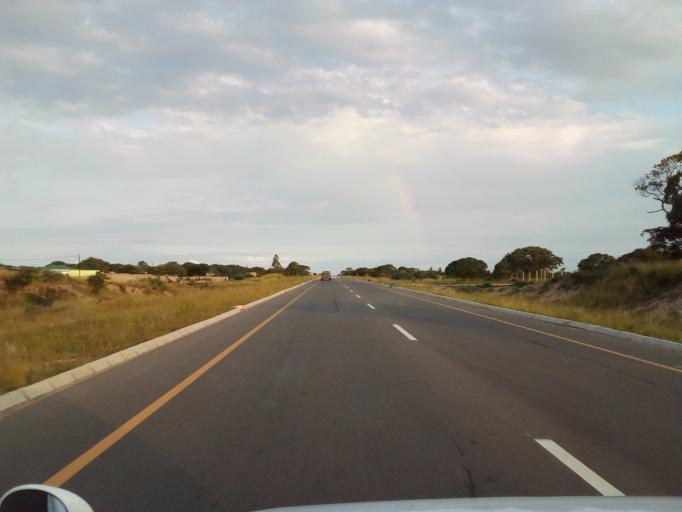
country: MZ
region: Maputo City
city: Maputo
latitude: -26.0582
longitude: 32.5898
